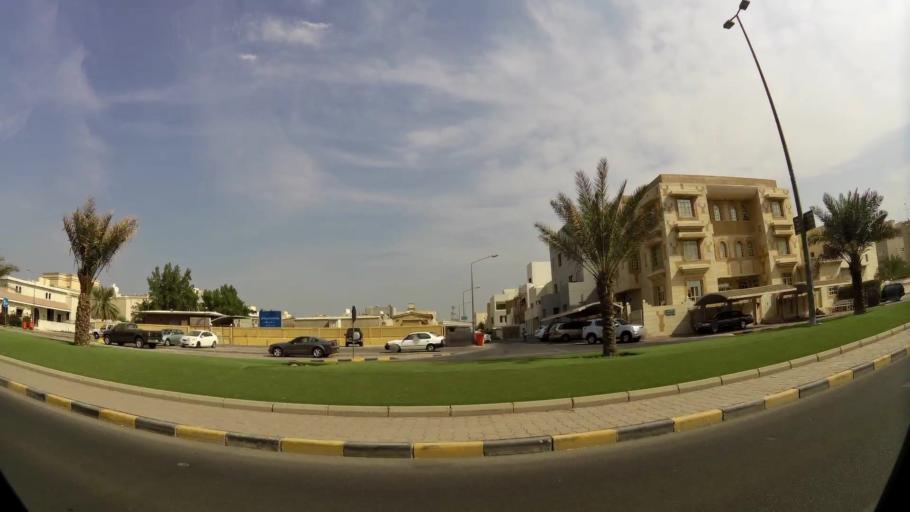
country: KW
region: Al Asimah
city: Ash Shamiyah
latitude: 29.3426
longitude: 47.9617
